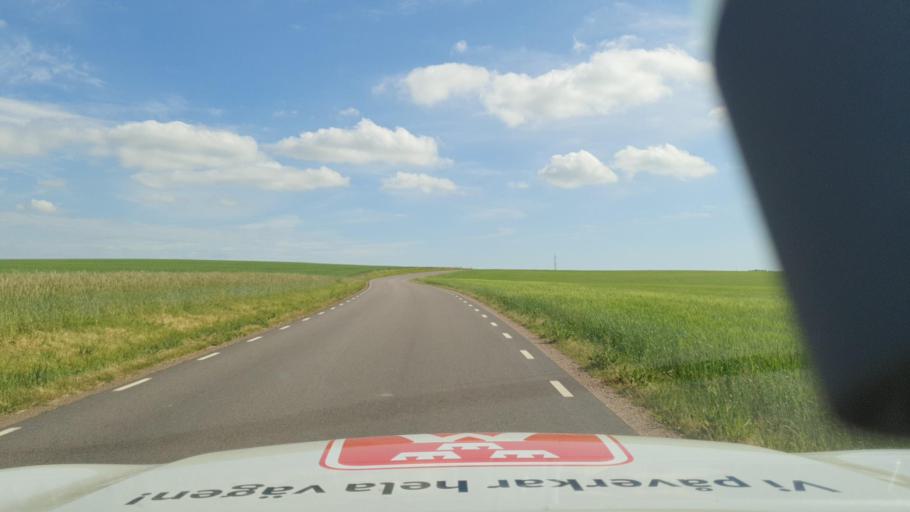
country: SE
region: Skane
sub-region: Sjobo Kommun
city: Blentarp
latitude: 55.5573
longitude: 13.5613
